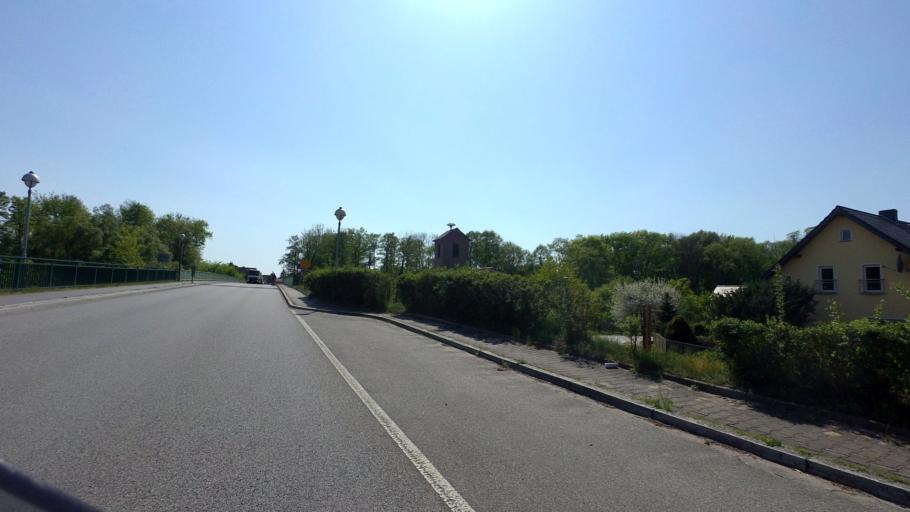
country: DE
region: Brandenburg
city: Tauche
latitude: 52.0859
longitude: 14.1710
